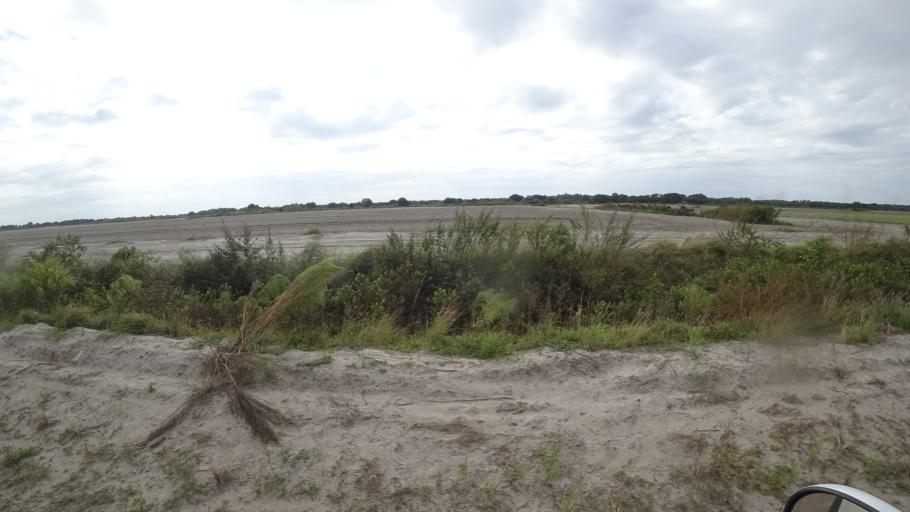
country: US
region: Florida
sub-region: Hillsborough County
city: Wimauma
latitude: 27.5625
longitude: -82.2991
